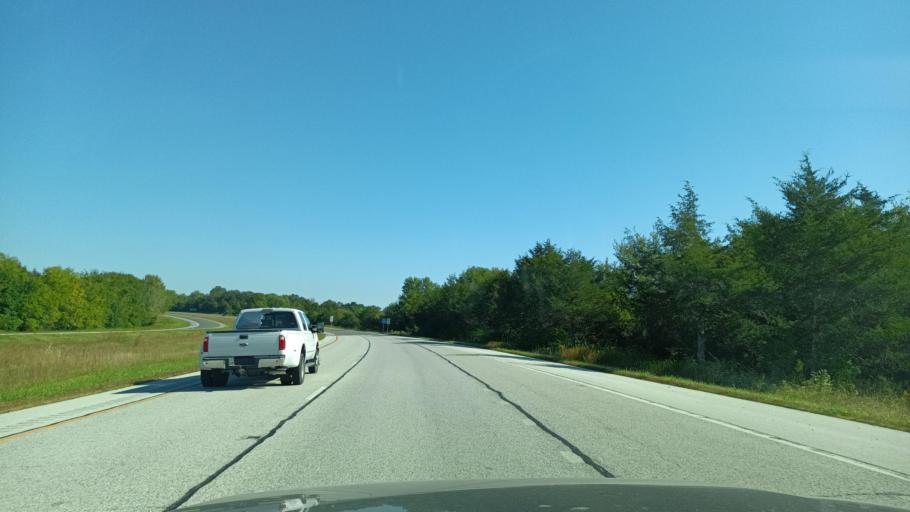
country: US
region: Illinois
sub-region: Adams County
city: Quincy
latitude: 39.8841
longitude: -91.3248
